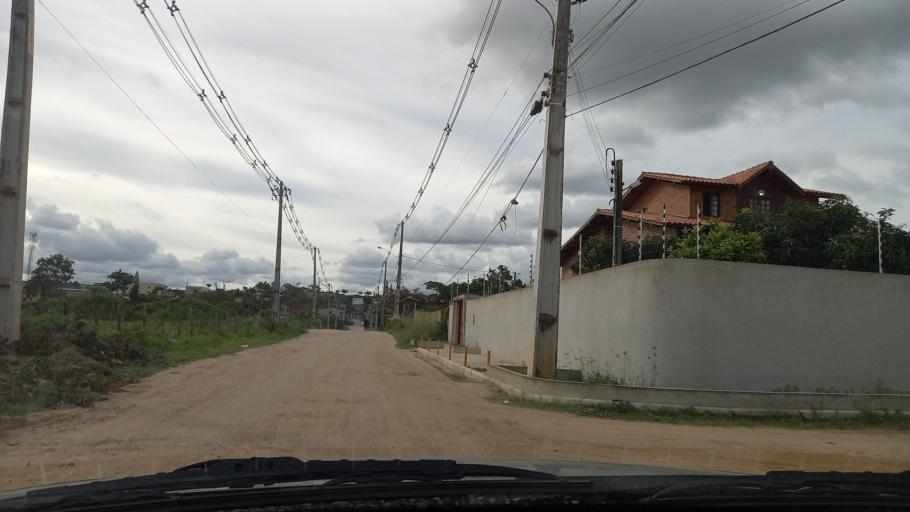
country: BR
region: Pernambuco
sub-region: Gravata
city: Gravata
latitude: -8.1991
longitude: -35.5494
